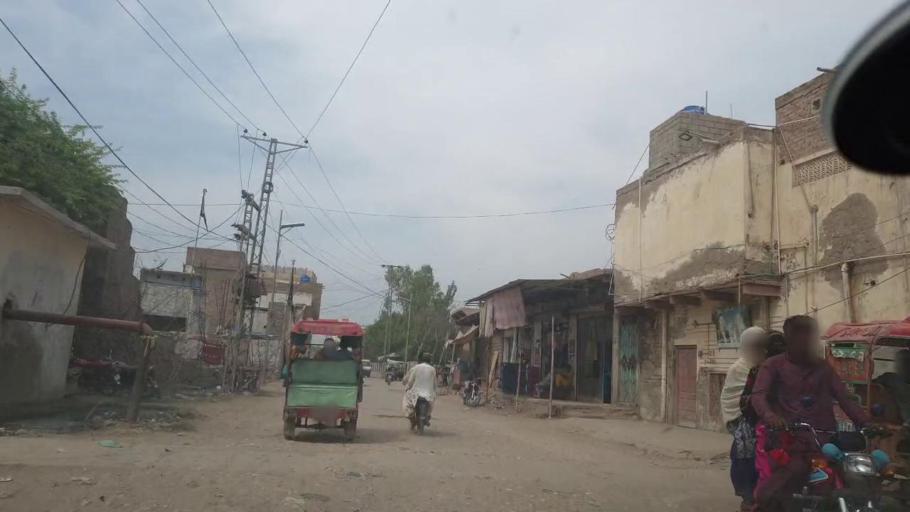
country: PK
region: Sindh
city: Jacobabad
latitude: 28.2769
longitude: 68.4382
